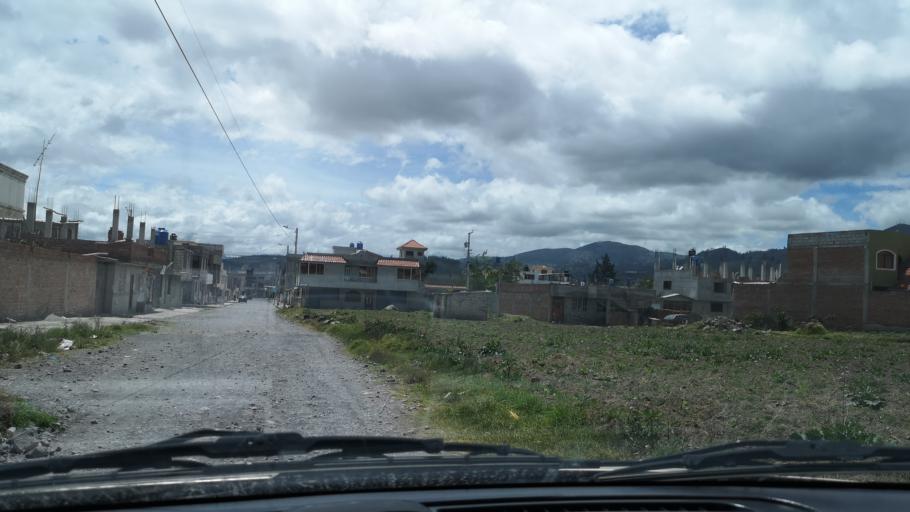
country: EC
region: Chimborazo
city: Riobamba
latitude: -1.6443
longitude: -78.6836
